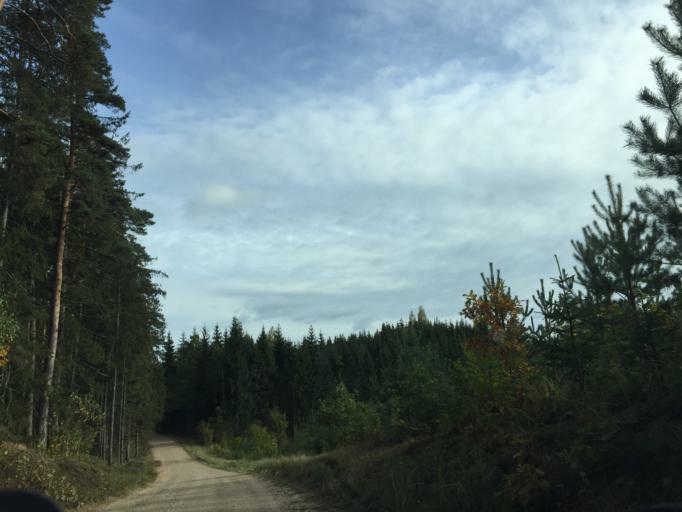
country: LV
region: Jaunpils
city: Jaunpils
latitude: 56.5831
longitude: 23.0196
